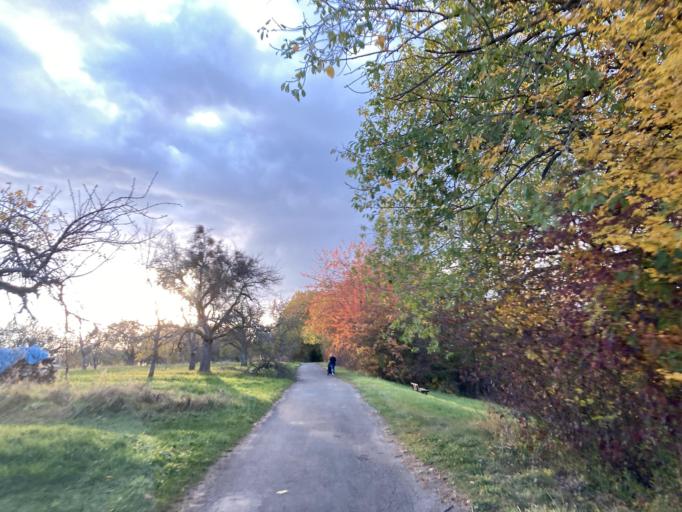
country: DE
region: Baden-Wuerttemberg
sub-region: Tuebingen Region
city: Gomaringen
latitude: 48.4609
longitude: 9.1232
